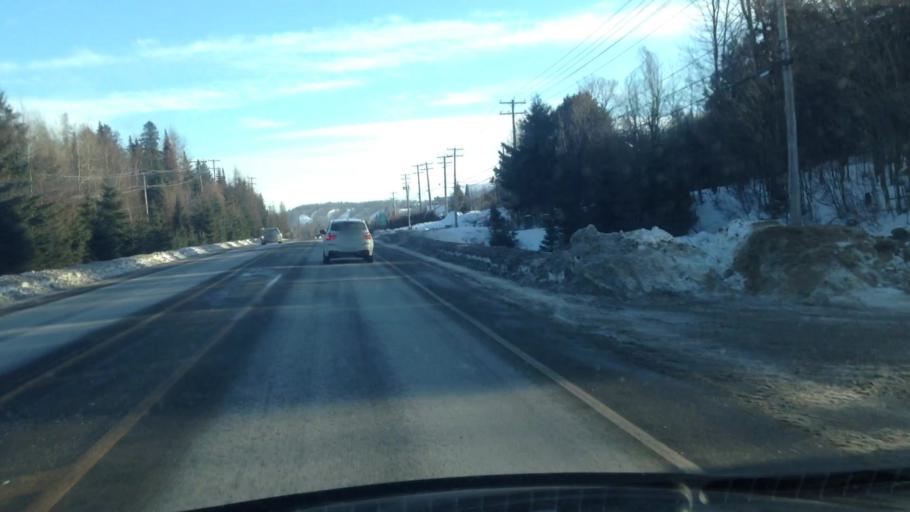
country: CA
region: Quebec
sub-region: Laurentides
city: Saint-Sauveur
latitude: 45.8915
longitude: -74.1943
